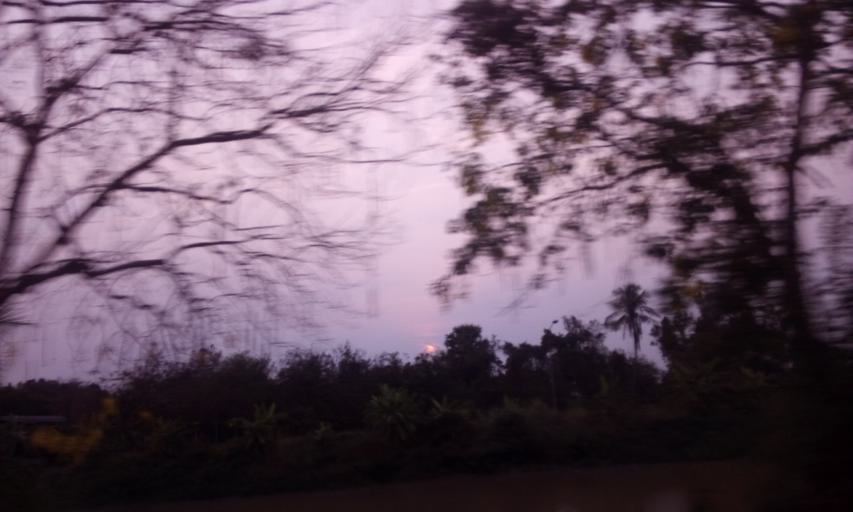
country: TH
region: Pathum Thani
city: Nong Suea
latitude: 14.0577
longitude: 100.8930
